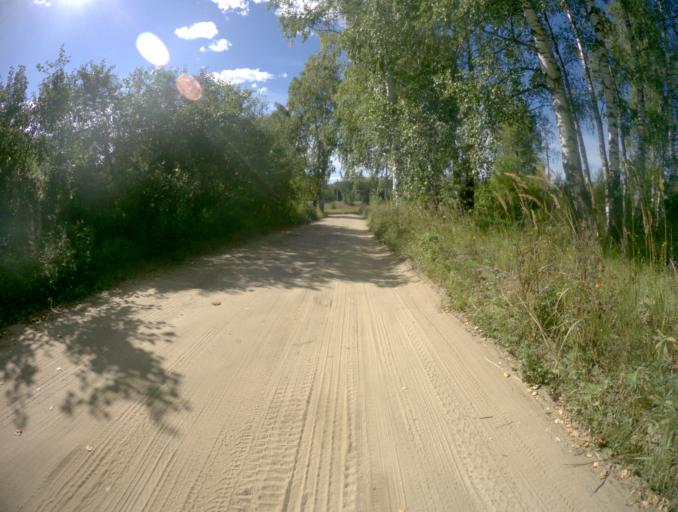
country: RU
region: Vladimir
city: Krasnaya Gorbatka
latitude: 55.8609
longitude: 41.7847
